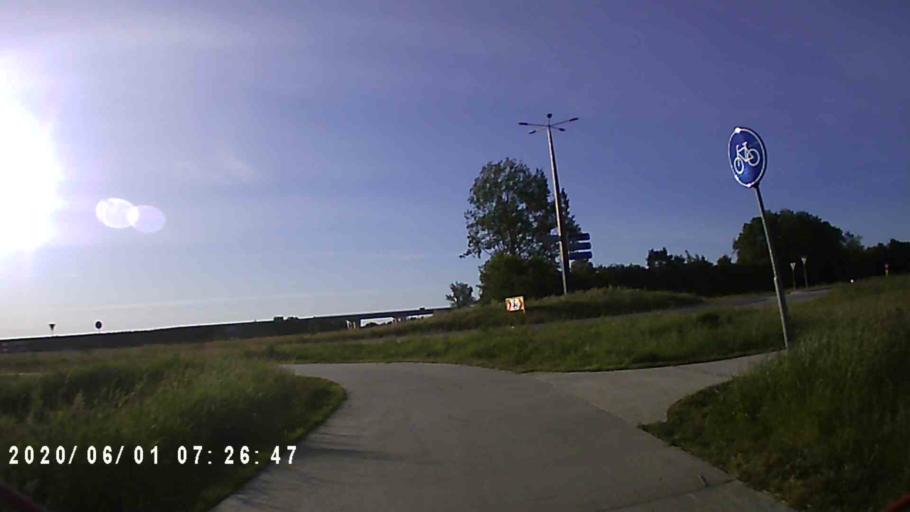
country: NL
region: Friesland
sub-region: Gemeente Dongeradeel
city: Dokkum
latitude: 53.3184
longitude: 6.0185
